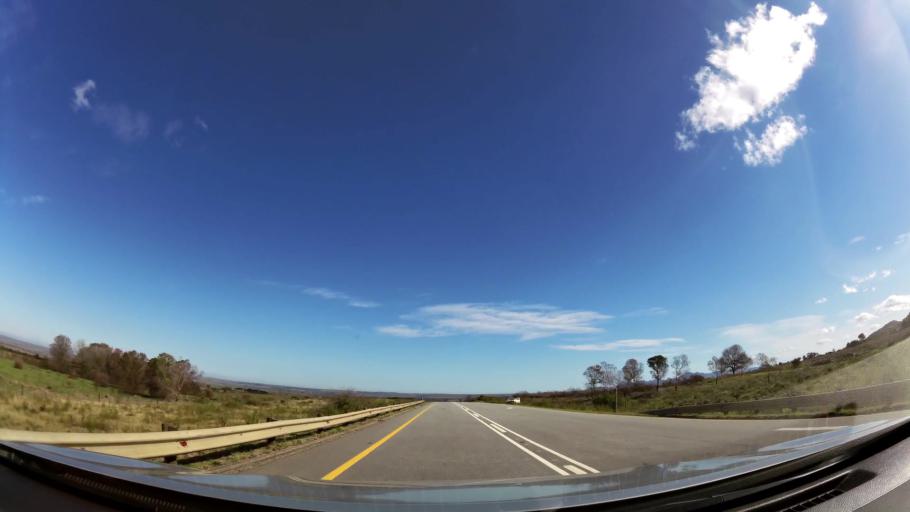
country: ZA
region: Eastern Cape
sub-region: Cacadu District Municipality
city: Kruisfontein
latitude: -33.9984
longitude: 24.6868
